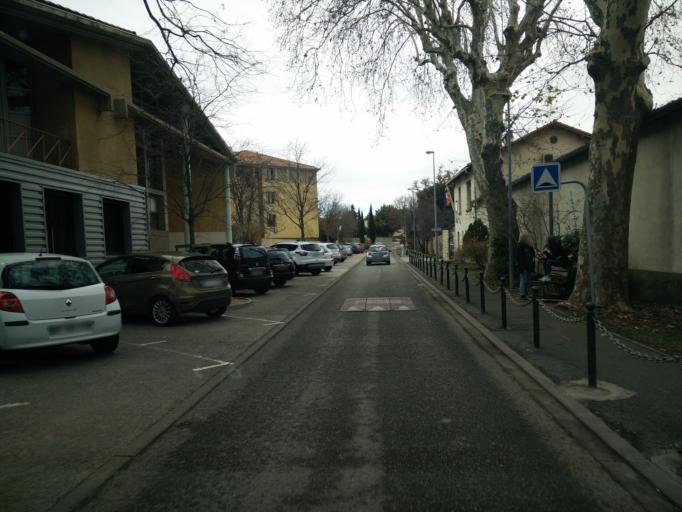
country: FR
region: Provence-Alpes-Cote d'Azur
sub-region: Departement du Var
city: Brignoles
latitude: 43.4116
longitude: 6.0660
